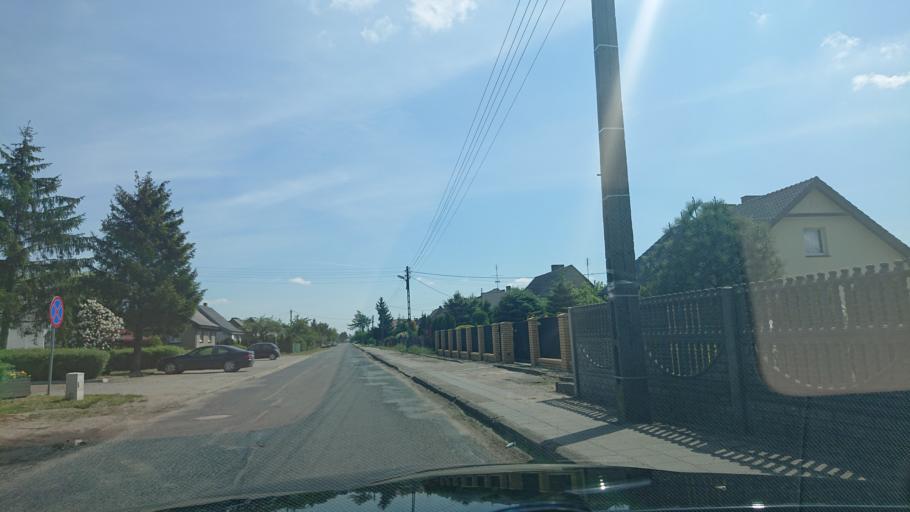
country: PL
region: Greater Poland Voivodeship
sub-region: Powiat gnieznienski
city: Gniezno
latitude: 52.4540
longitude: 17.5933
